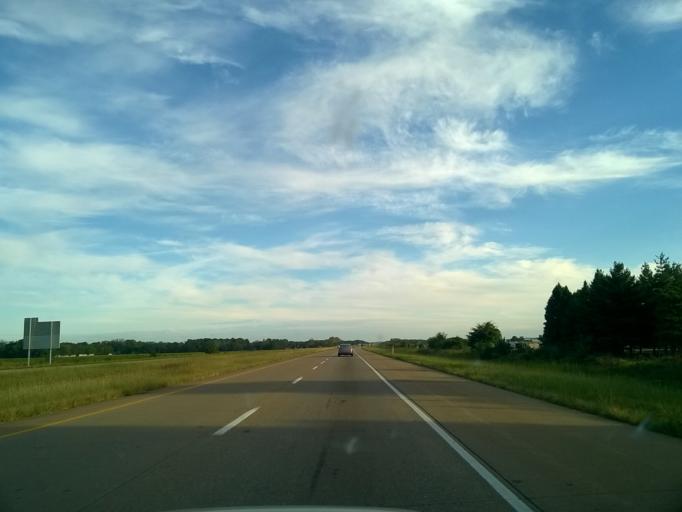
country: US
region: Indiana
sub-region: Vanderburgh County
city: Melody Hill
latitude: 38.0382
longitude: -87.4734
